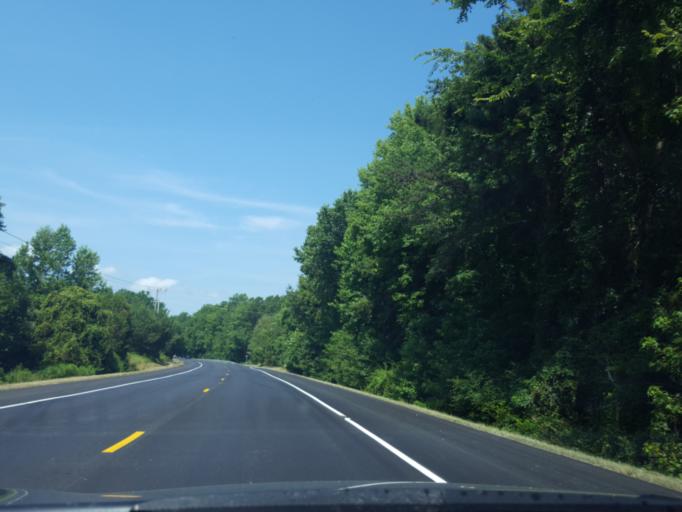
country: US
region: Maryland
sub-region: Saint Mary's County
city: Charlotte Hall
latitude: 38.4119
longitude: -76.8686
